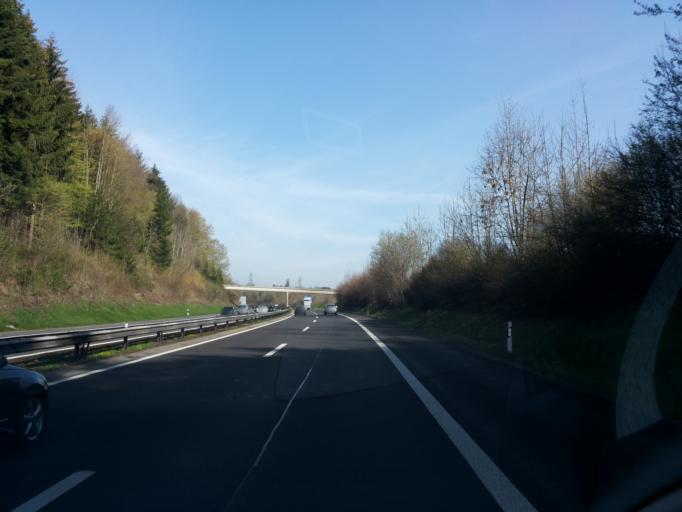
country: CH
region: Lucerne
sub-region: Hochdorf District
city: Emmen
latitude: 47.1009
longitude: 8.2454
